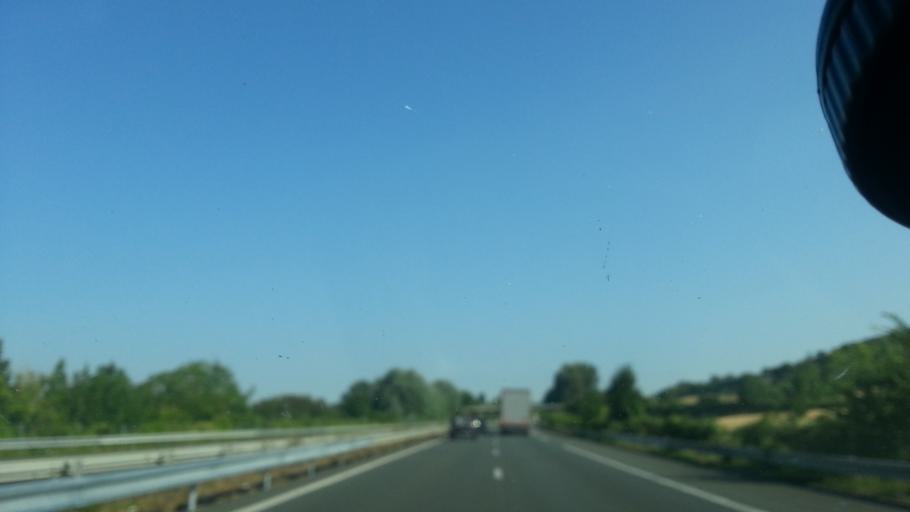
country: FR
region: Poitou-Charentes
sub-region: Departement de la Vienne
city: Antran
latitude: 46.8745
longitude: 0.5200
